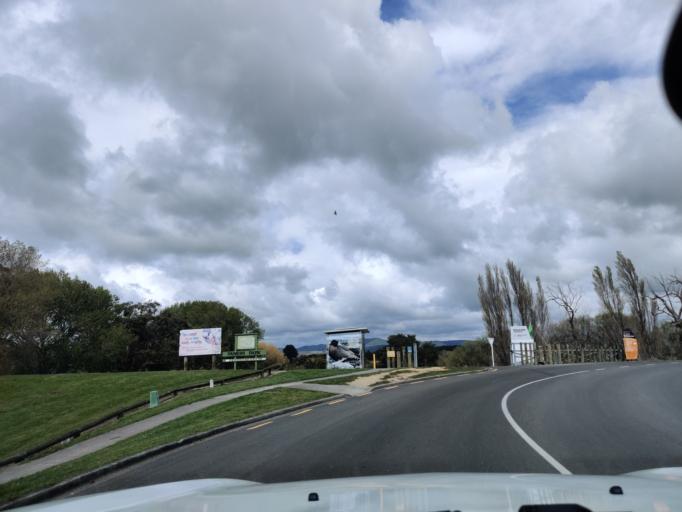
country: NZ
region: Manawatu-Wanganui
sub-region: Palmerston North City
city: Palmerston North
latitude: -40.3820
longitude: 175.5867
